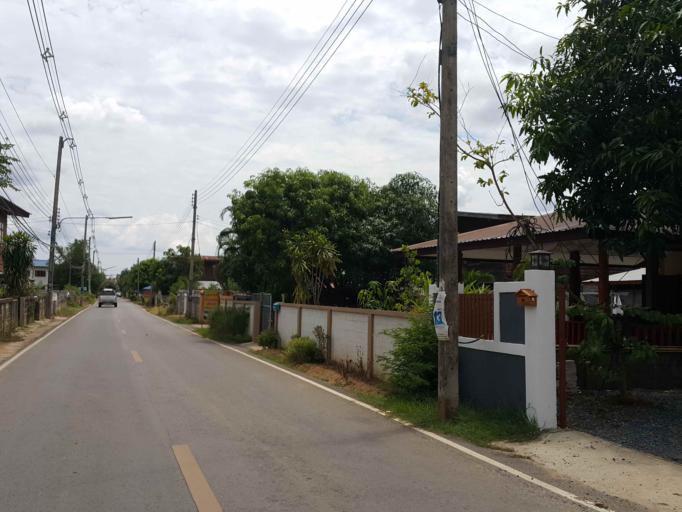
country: TH
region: Sukhothai
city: Thung Saliam
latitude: 17.3196
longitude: 99.5482
